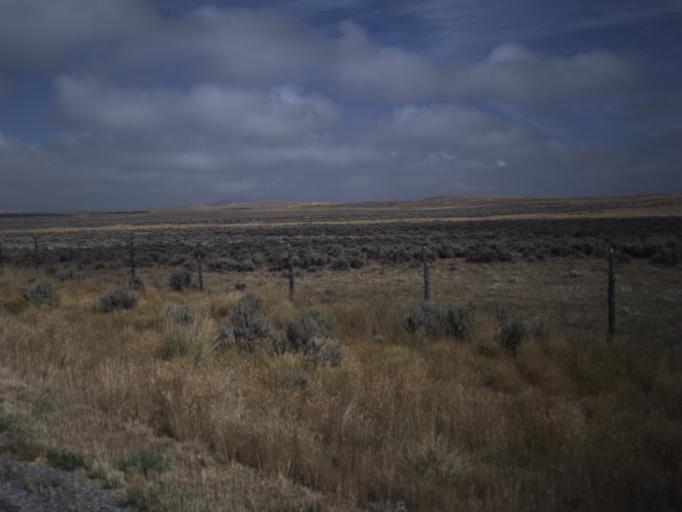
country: US
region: Wyoming
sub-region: Uinta County
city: Evanston
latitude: 41.4504
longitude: -111.0859
